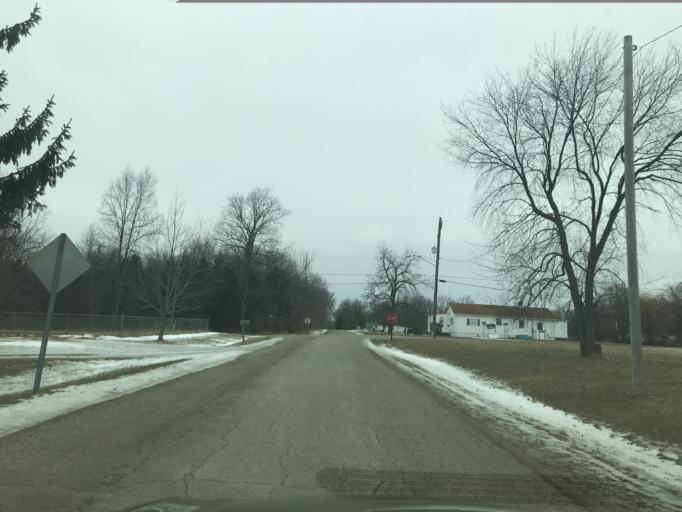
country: US
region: Michigan
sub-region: Jackson County
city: Brooklyn
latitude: 42.0663
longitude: -84.3330
